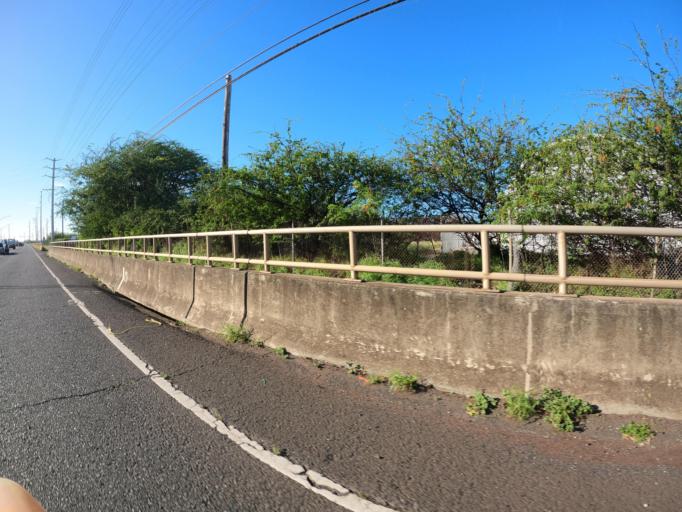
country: US
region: Hawaii
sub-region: Honolulu County
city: Honolulu
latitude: 21.3115
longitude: -157.8869
